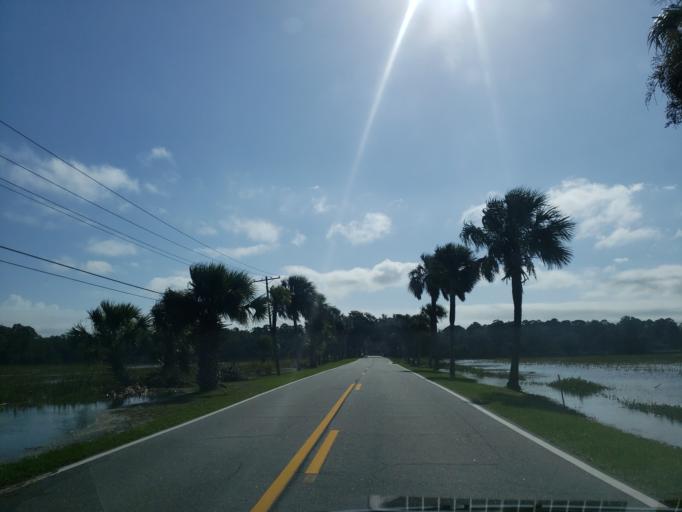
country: US
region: Georgia
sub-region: Chatham County
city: Montgomery
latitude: 31.9356
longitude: -81.1015
